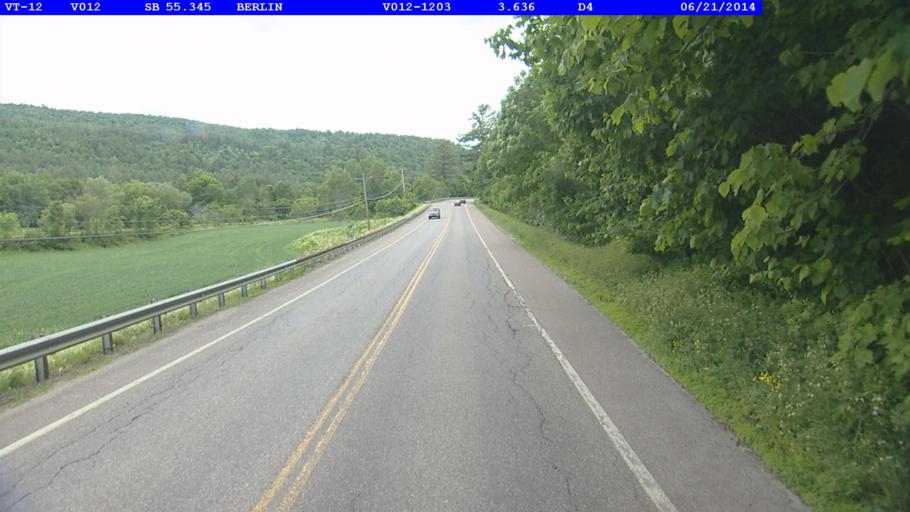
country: US
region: Vermont
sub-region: Washington County
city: Montpelier
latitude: 44.2190
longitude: -72.6251
